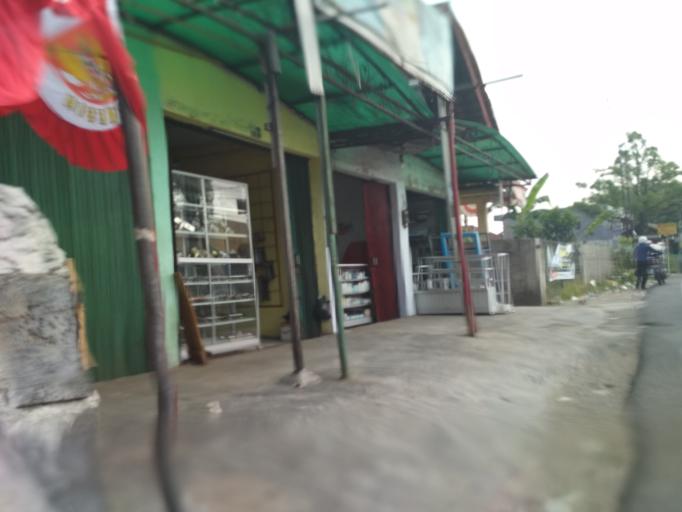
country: ID
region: West Java
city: Bogor
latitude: -6.5727
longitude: 106.7473
